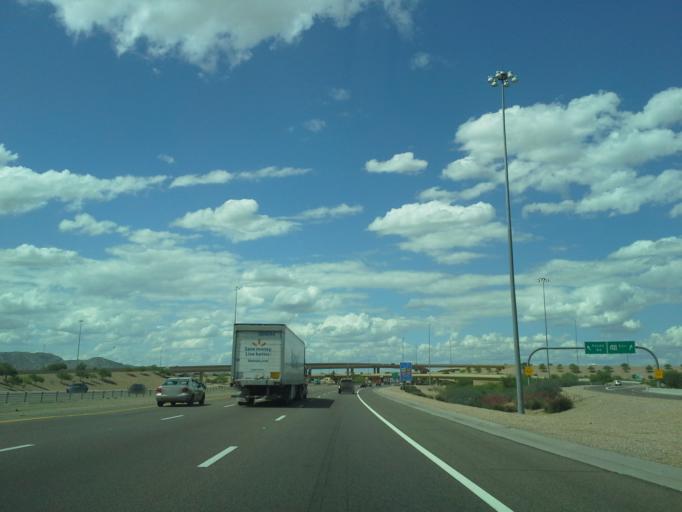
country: US
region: Arizona
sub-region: Maricopa County
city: Guadalupe
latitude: 33.2919
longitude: -111.9716
